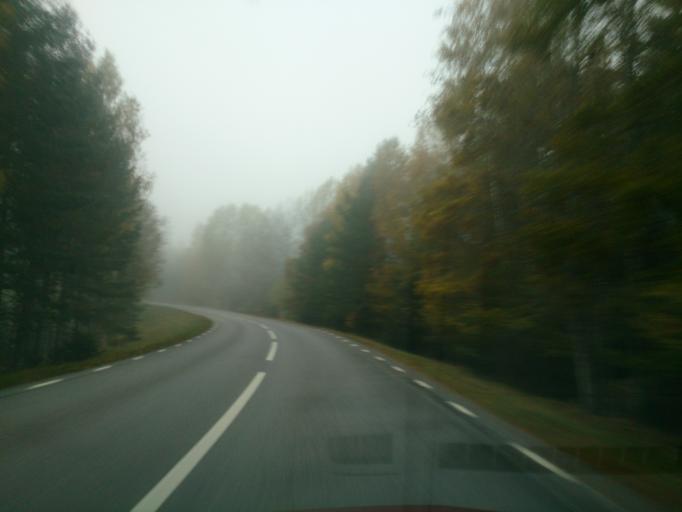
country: SE
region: OEstergoetland
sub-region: Atvidabergs Kommun
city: Atvidaberg
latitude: 58.1273
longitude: 15.9533
